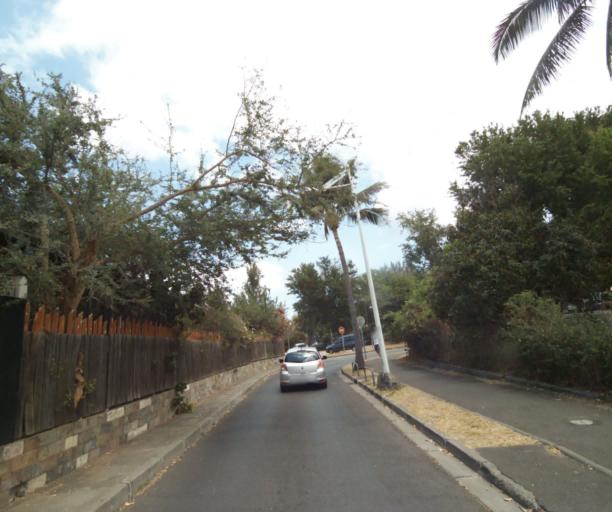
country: RE
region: Reunion
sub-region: Reunion
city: Saint-Paul
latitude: -21.0699
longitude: 55.2233
